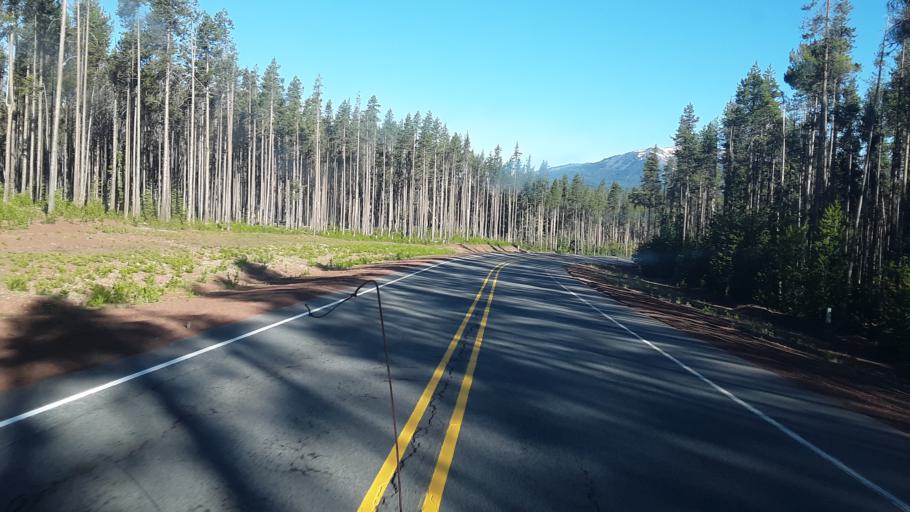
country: US
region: Oregon
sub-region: Lane County
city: Oakridge
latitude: 43.0995
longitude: -122.1277
